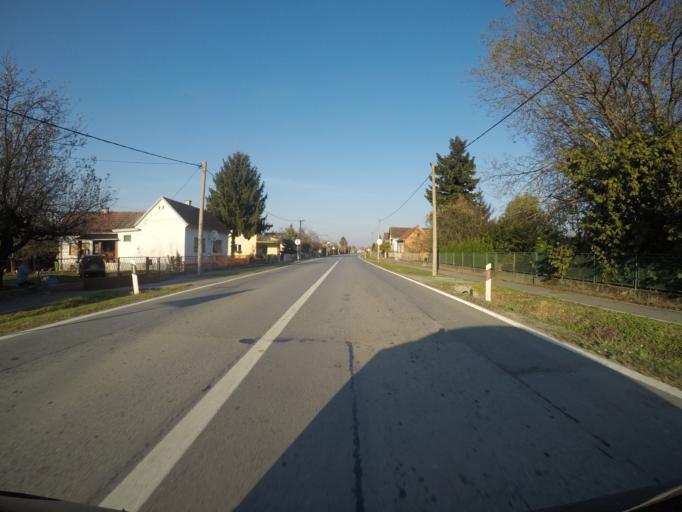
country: HU
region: Somogy
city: Barcs
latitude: 45.8938
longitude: 17.4307
